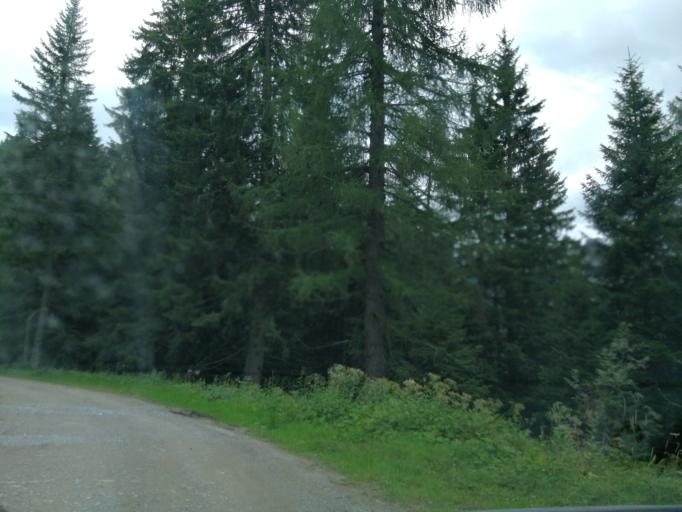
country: IT
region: Trentino-Alto Adige
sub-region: Provincia di Trento
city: Castel Condino
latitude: 45.9396
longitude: 10.5620
